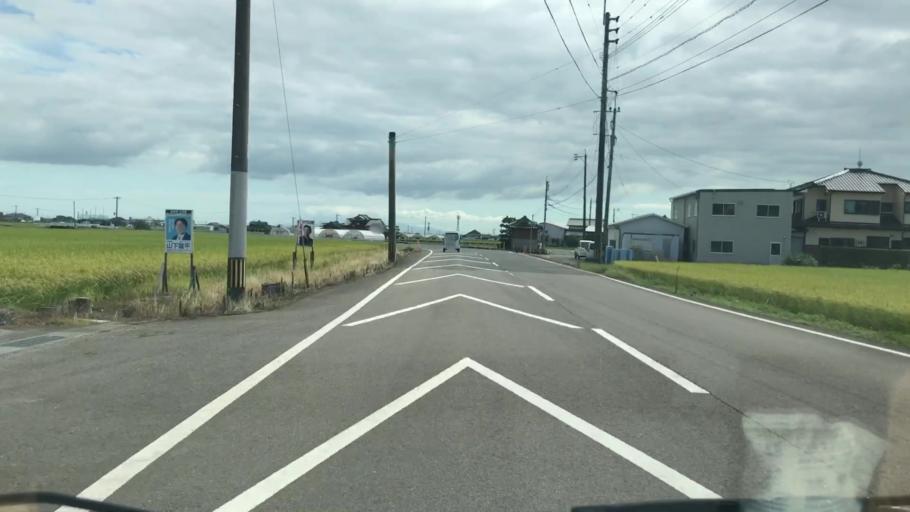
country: JP
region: Saga Prefecture
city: Saga-shi
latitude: 33.1974
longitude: 130.1814
